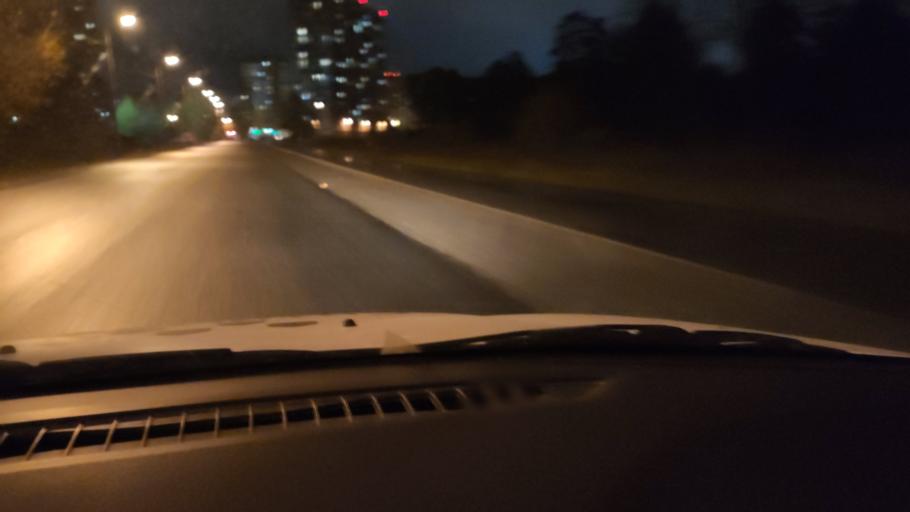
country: RU
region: Perm
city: Kondratovo
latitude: 57.9897
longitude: 56.1357
